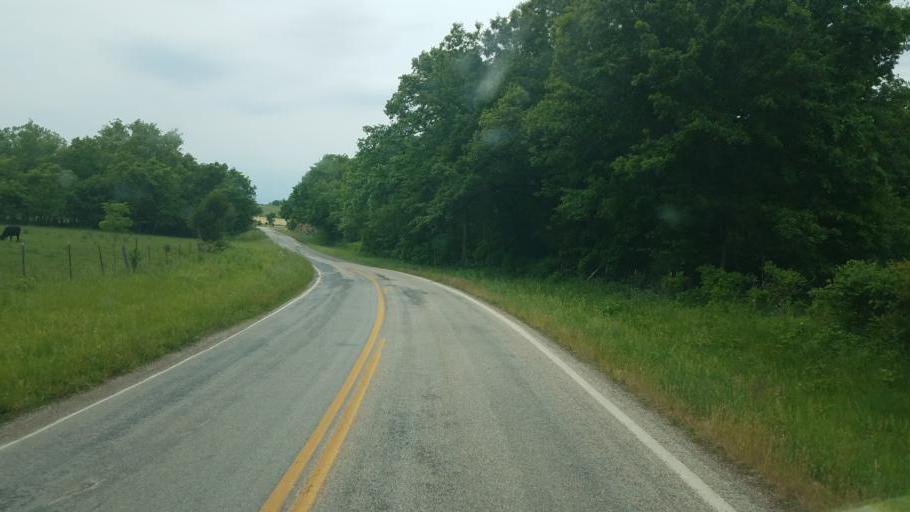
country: US
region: Missouri
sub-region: Moniteau County
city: California
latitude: 38.6875
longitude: -92.6126
